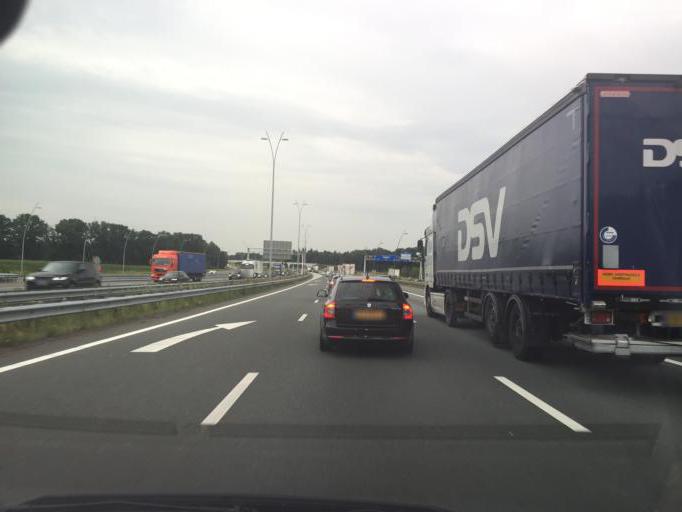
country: NL
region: North Brabant
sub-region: Gemeente Eindhoven
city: Meerhoven
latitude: 51.4658
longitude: 5.4057
